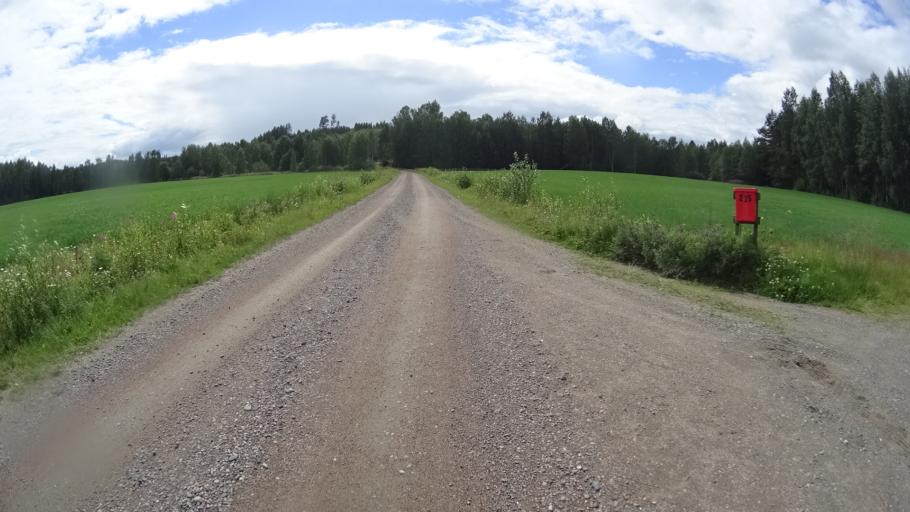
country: FI
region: Uusimaa
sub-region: Helsinki
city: Karkkila
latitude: 60.5831
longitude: 24.3011
